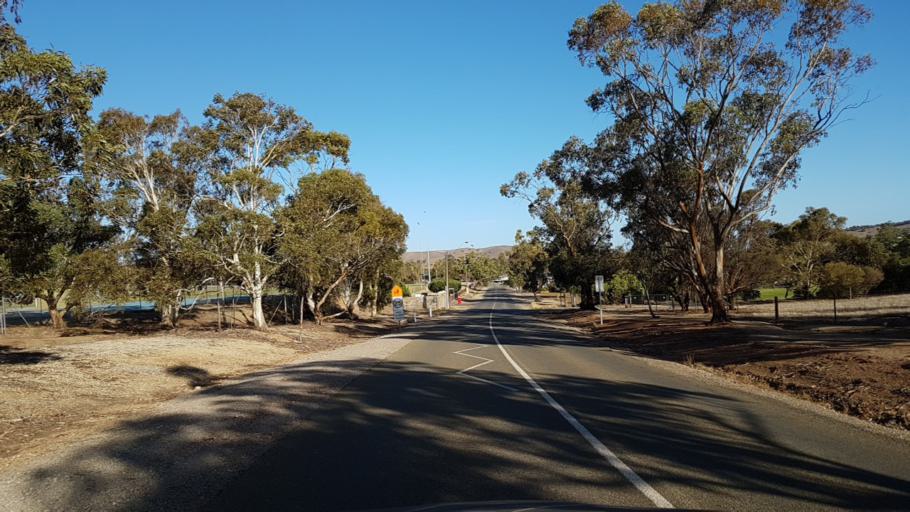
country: AU
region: South Australia
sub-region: Clare and Gilbert Valleys
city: Clare
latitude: -33.6752
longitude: 138.9393
